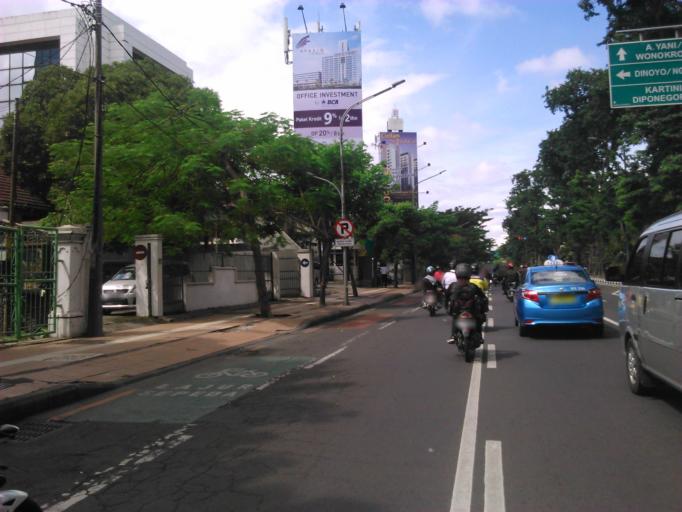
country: ID
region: East Java
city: Gubengairlangga
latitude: -7.2785
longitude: 112.7411
